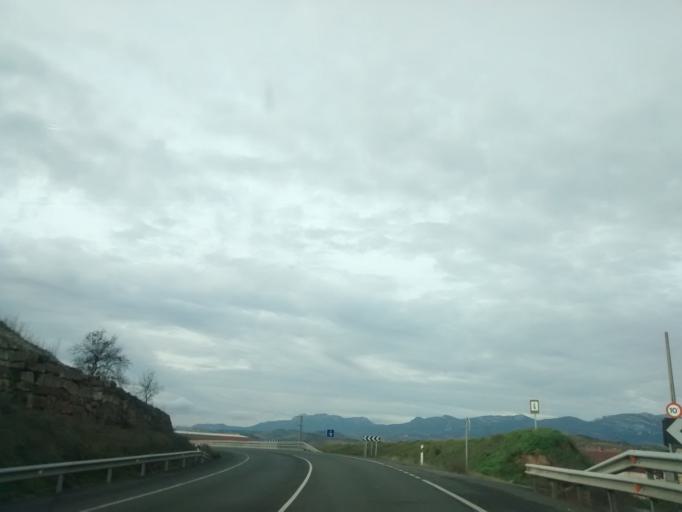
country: ES
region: La Rioja
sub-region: Provincia de La Rioja
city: Cenicero
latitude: 42.4792
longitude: -2.6438
